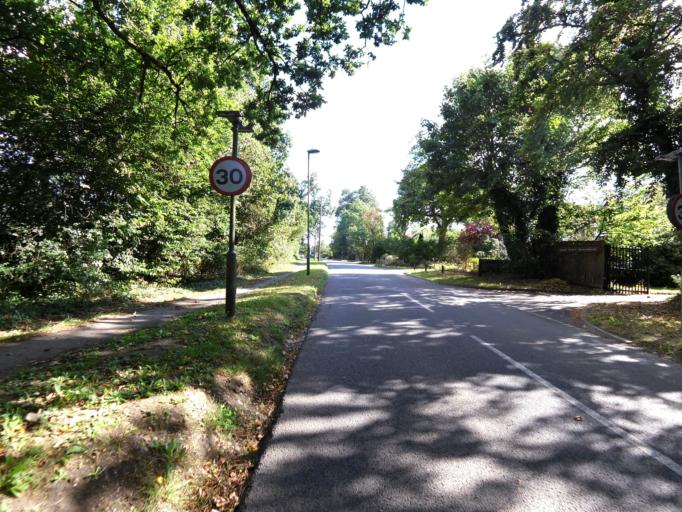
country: GB
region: England
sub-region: Greater London
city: High Barnet
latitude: 51.6588
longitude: -0.2281
